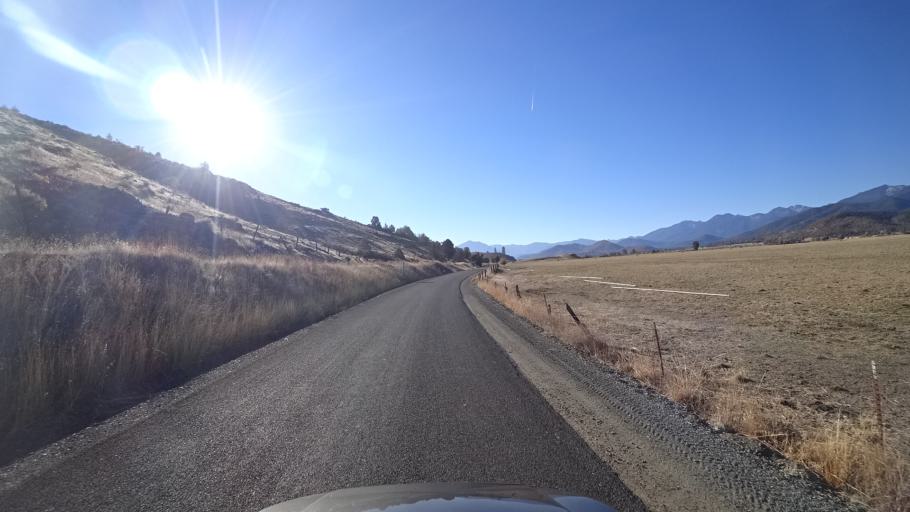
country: US
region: California
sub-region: Siskiyou County
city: Yreka
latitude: 41.4511
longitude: -122.8472
